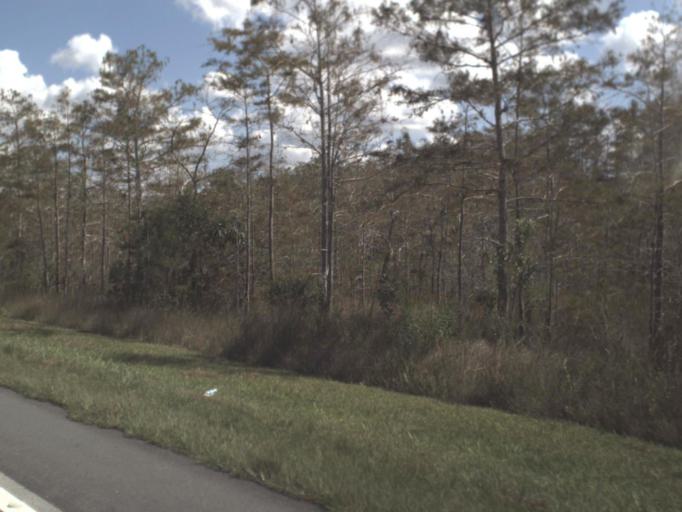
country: US
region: Florida
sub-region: Miami-Dade County
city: Kendall West
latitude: 25.8496
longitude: -80.9621
